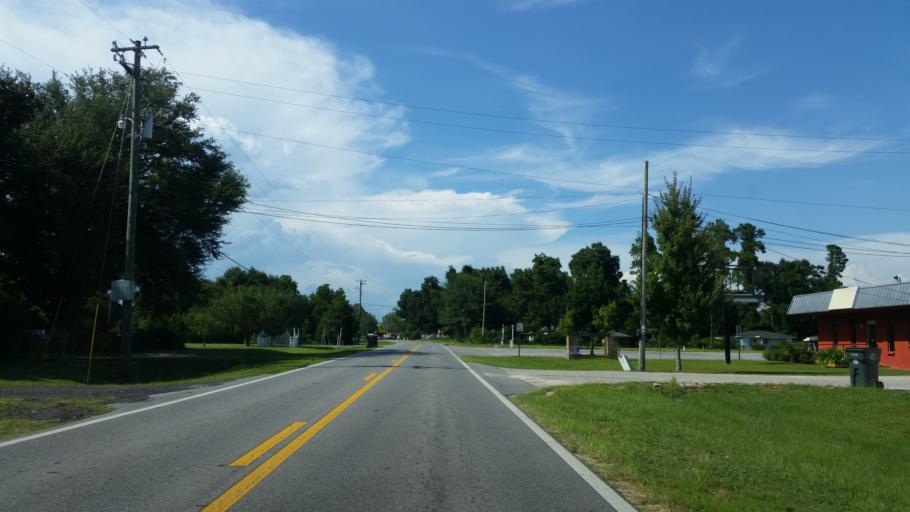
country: US
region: Florida
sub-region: Santa Rosa County
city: Pace
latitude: 30.5958
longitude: -87.1611
